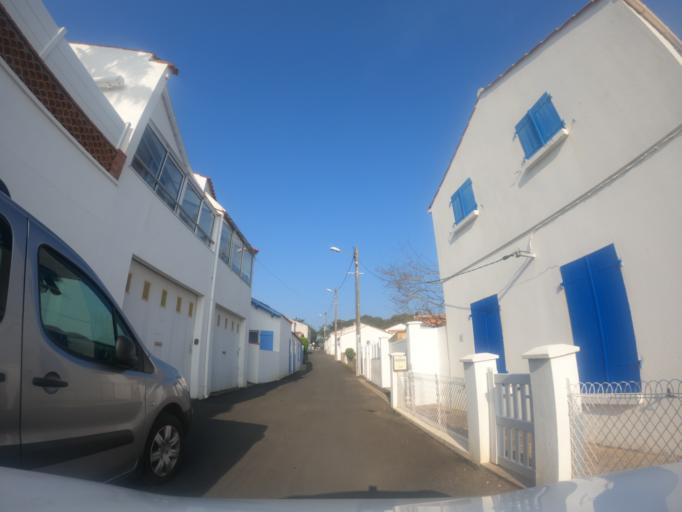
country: FR
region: Pays de la Loire
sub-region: Departement de la Vendee
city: La Tranche-sur-Mer
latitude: 46.3446
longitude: -1.4418
